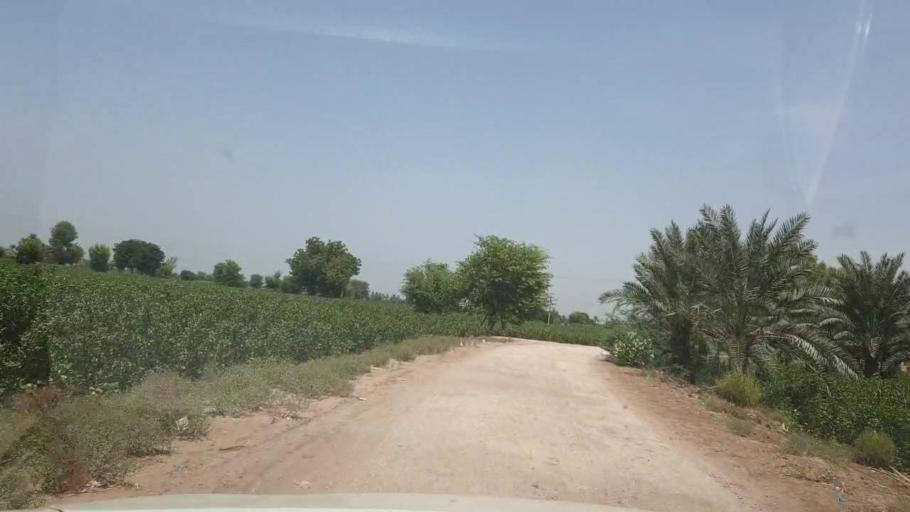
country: PK
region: Sindh
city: Bozdar
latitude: 27.1600
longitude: 68.6152
